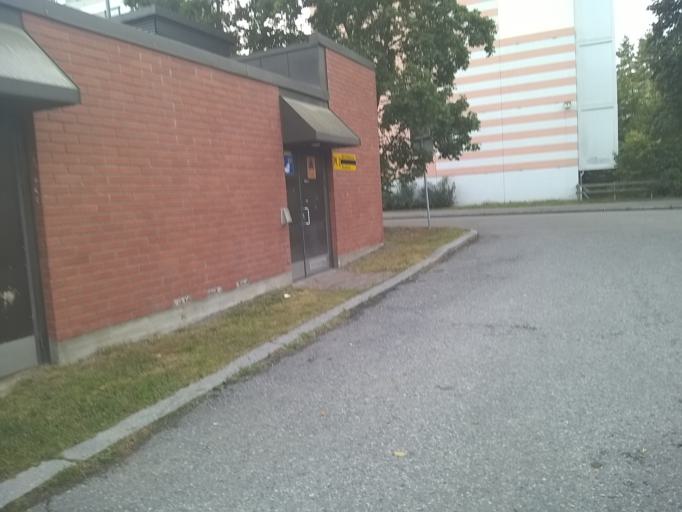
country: FI
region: Pirkanmaa
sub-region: Tampere
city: Tampere
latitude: 61.4449
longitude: 23.8483
